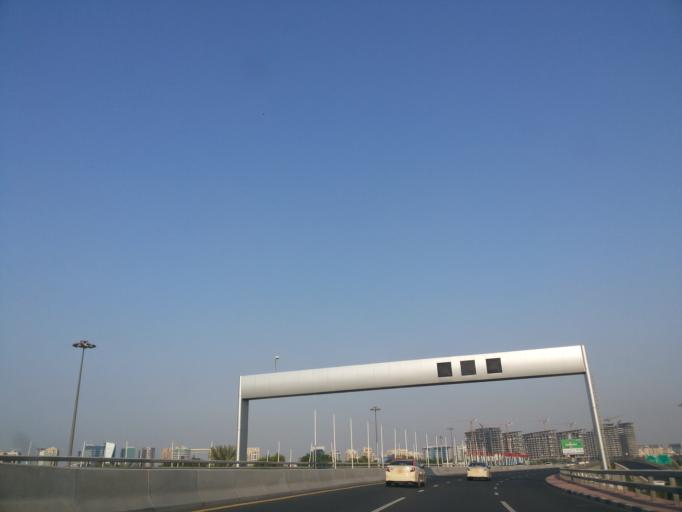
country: AE
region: Ash Shariqah
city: Sharjah
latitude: 25.2482
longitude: 55.3151
